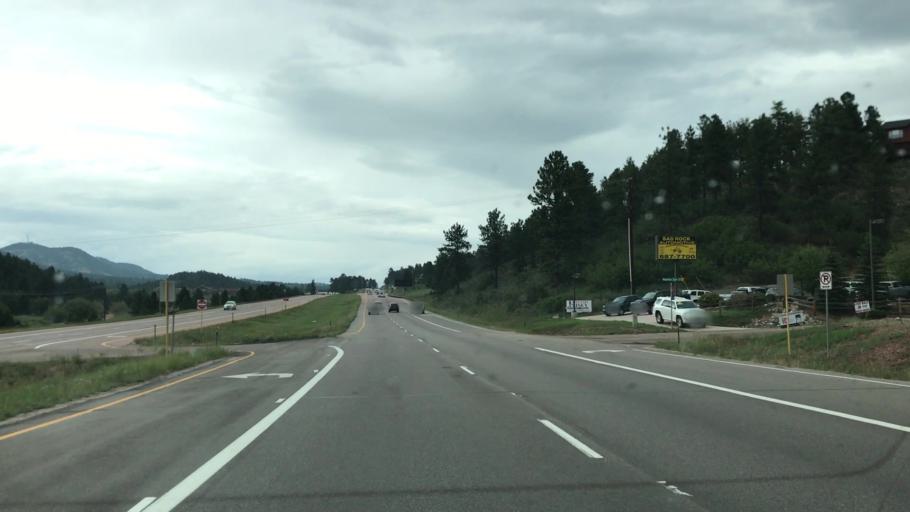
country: US
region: Colorado
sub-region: El Paso County
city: Cascade-Chipita Park
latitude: 38.9628
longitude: -105.0301
